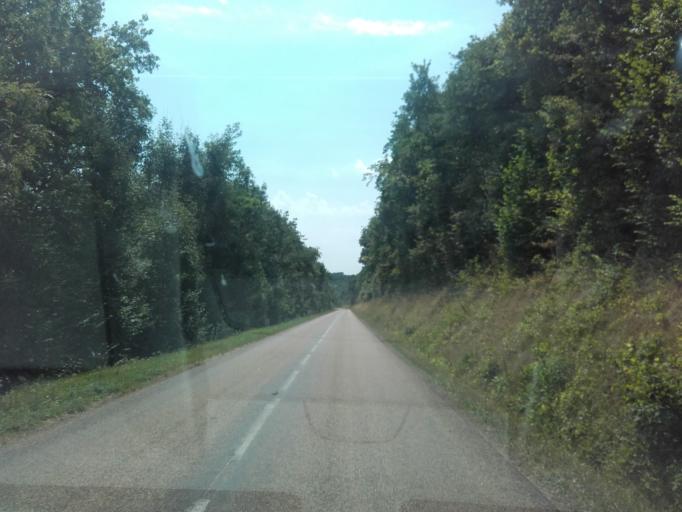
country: FR
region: Bourgogne
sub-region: Departement de l'Yonne
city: Chablis
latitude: 47.8403
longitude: 3.8353
